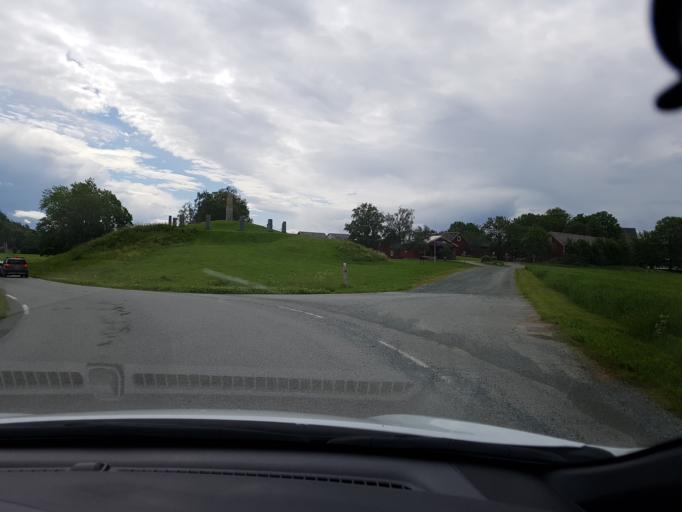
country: NO
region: Nord-Trondelag
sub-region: Frosta
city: Frosta
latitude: 63.5691
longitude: 10.7038
